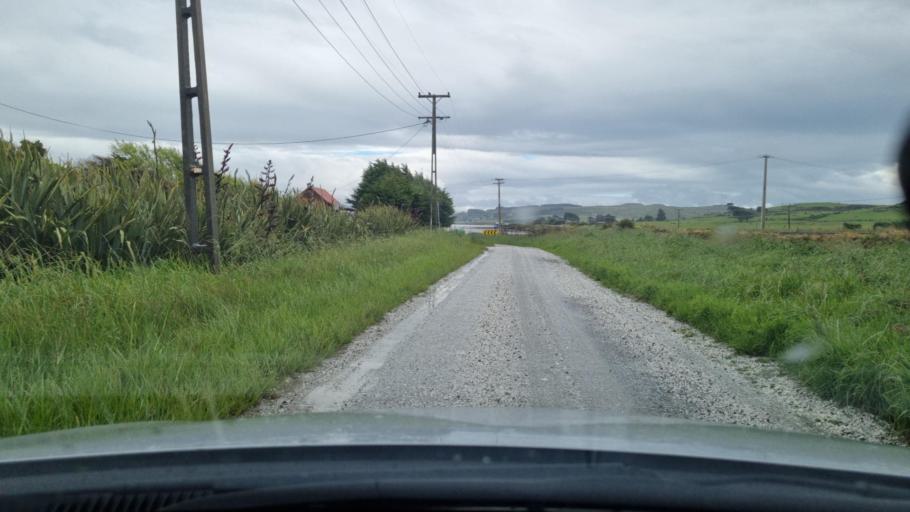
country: NZ
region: Southland
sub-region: Invercargill City
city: Bluff
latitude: -46.5476
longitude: 168.3013
